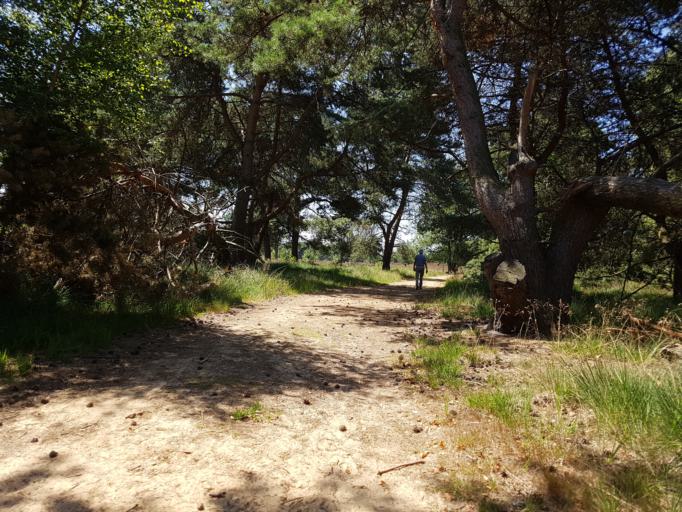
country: NL
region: North Brabant
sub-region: Gemeente Haaren
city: Haaren
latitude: 51.5771
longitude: 5.2562
